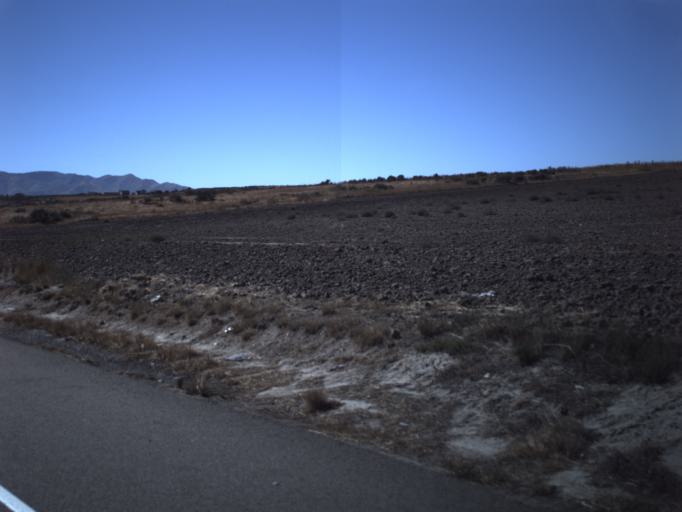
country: US
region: Utah
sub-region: Utah County
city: Saratoga Springs
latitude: 40.4179
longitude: -111.9246
